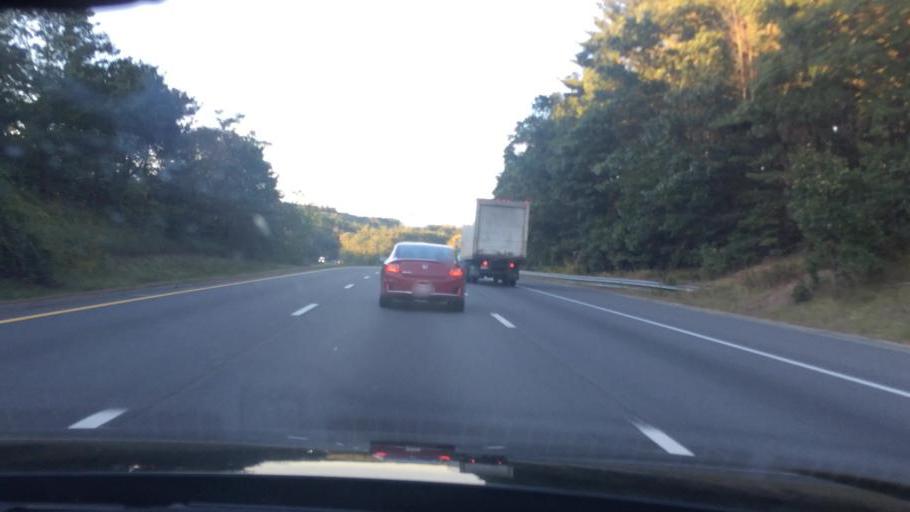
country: US
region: Massachusetts
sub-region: Middlesex County
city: Tewksbury
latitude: 42.6556
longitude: -71.2050
